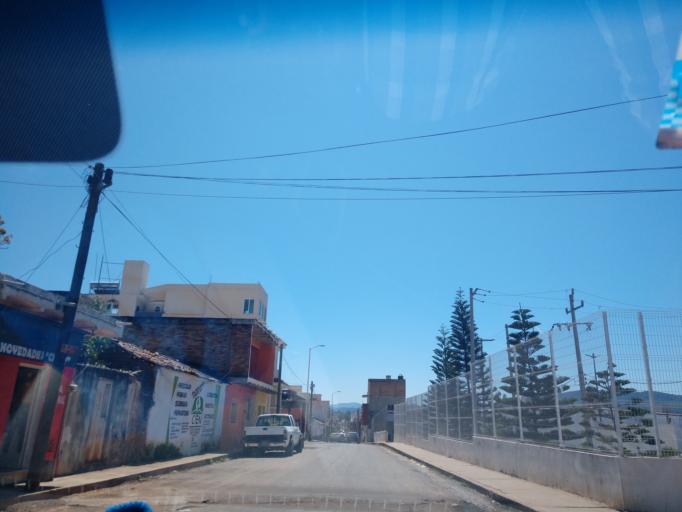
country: MX
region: Nayarit
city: Compostela
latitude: 21.2402
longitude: -104.8993
